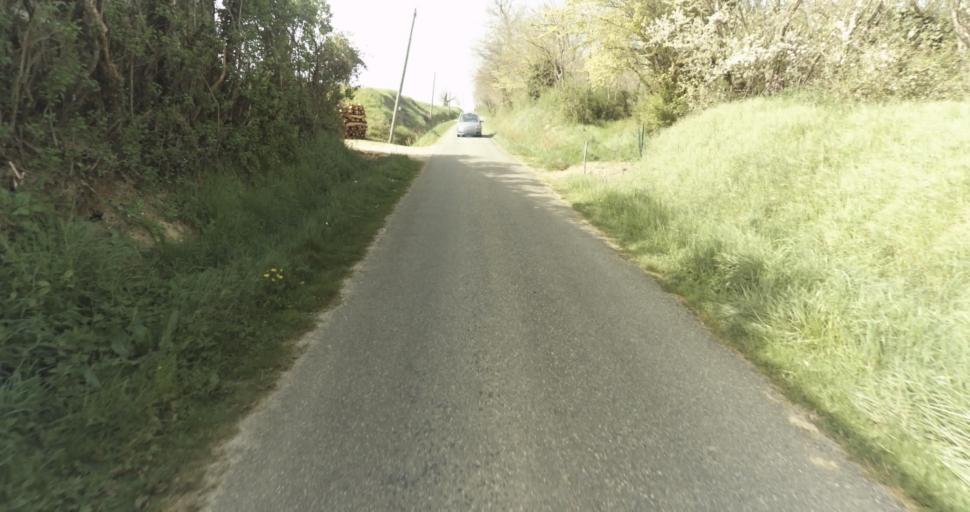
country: FR
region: Midi-Pyrenees
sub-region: Departement du Tarn-et-Garonne
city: Moissac
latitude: 44.1383
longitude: 1.1531
